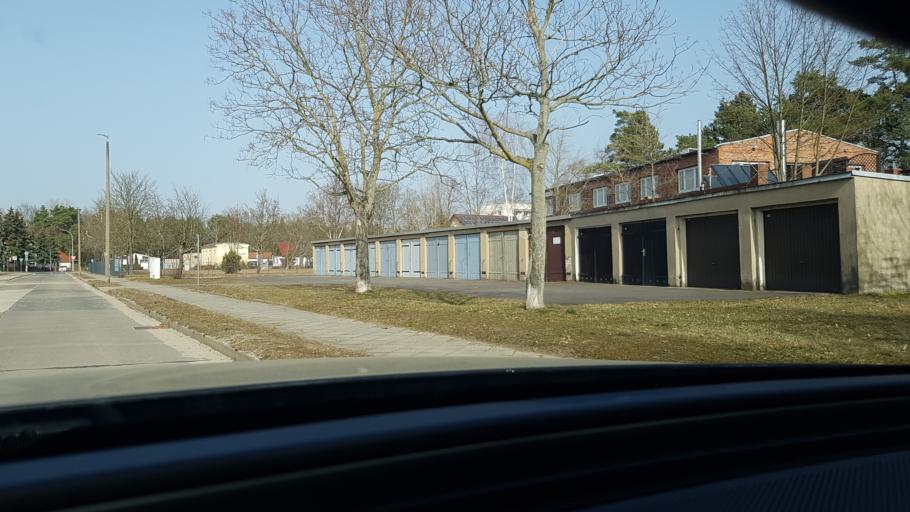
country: DE
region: Brandenburg
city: Guben
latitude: 51.9385
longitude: 14.6979
